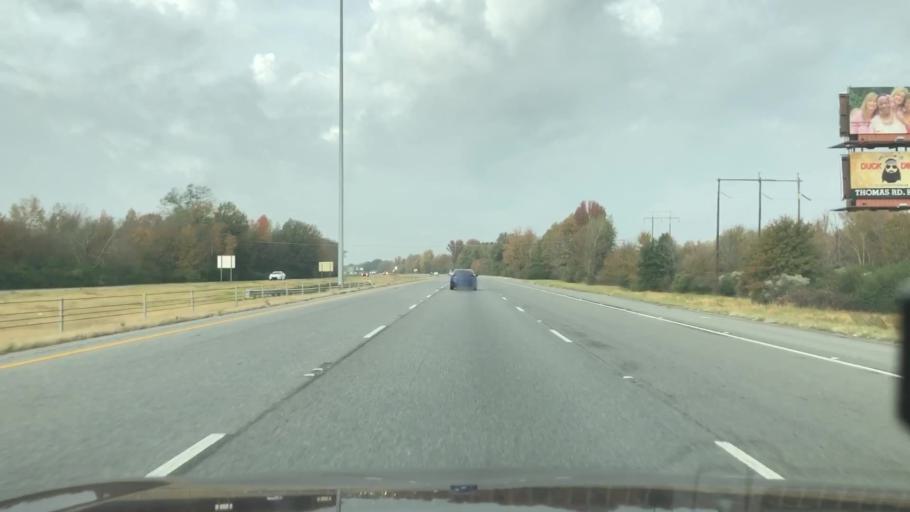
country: US
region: Louisiana
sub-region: Richland Parish
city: Delhi
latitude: 32.4441
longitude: -91.4990
